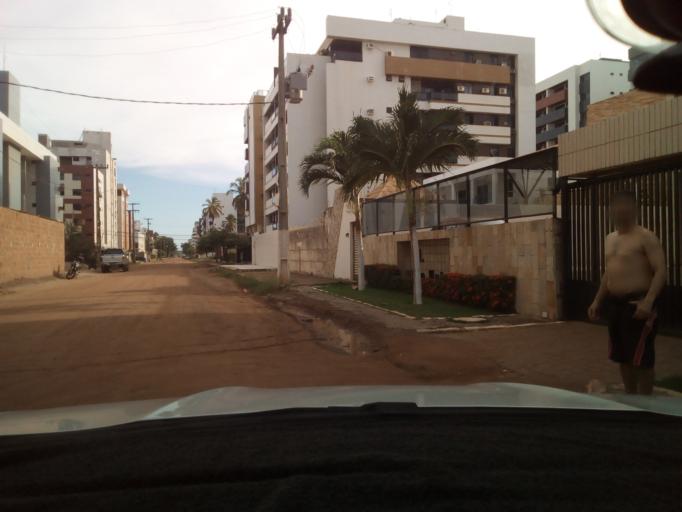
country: BR
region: Paraiba
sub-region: Cabedelo
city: Cabedelo
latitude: -7.0368
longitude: -34.8382
